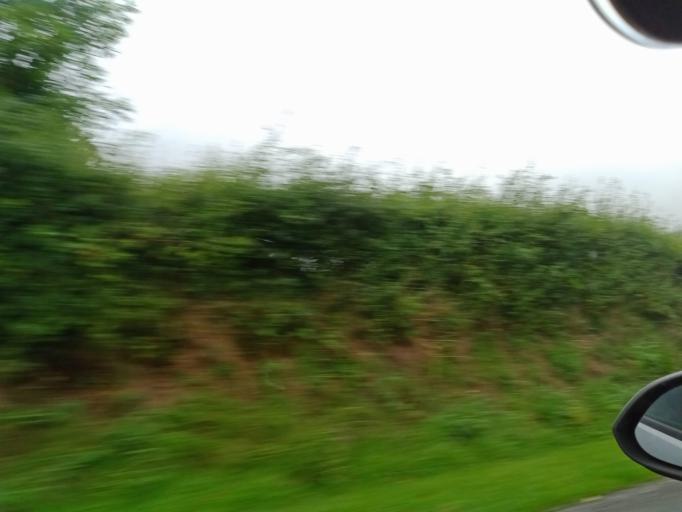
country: IE
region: Leinster
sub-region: Kilkenny
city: Castlecomer
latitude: 52.8541
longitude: -7.1726
